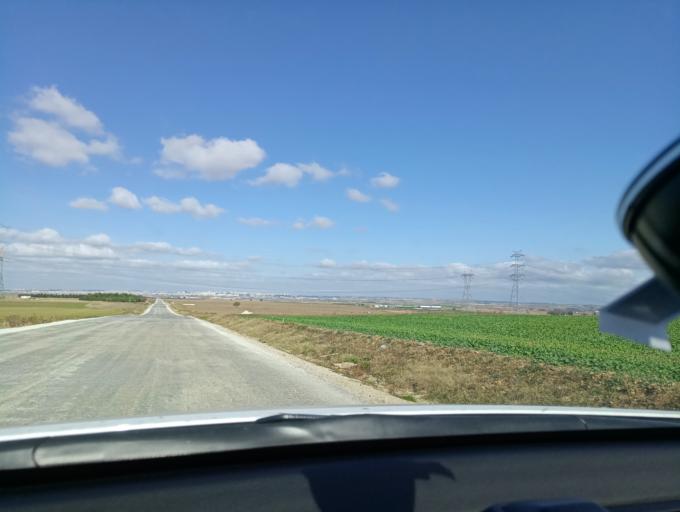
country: TR
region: Tekirdag
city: Corlu
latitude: 41.0576
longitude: 27.8347
